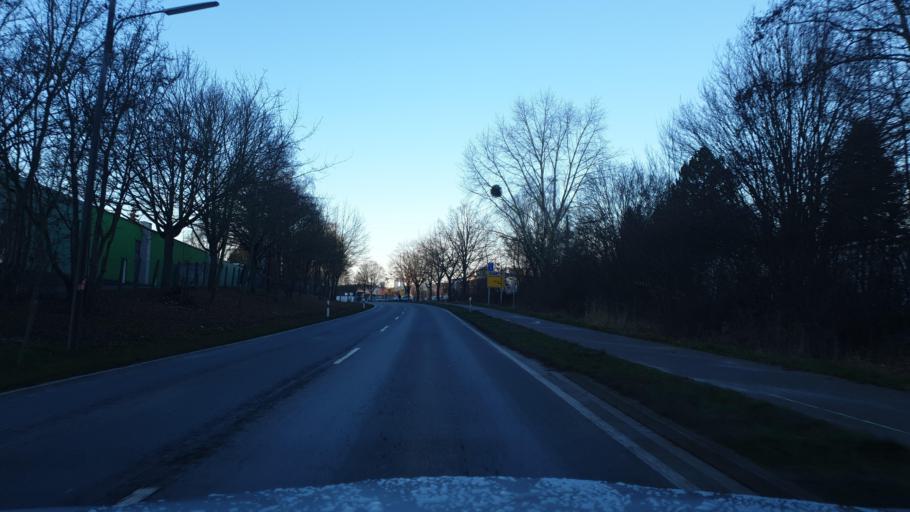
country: DE
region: North Rhine-Westphalia
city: Bad Oeynhausen
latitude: 52.2095
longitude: 8.8412
